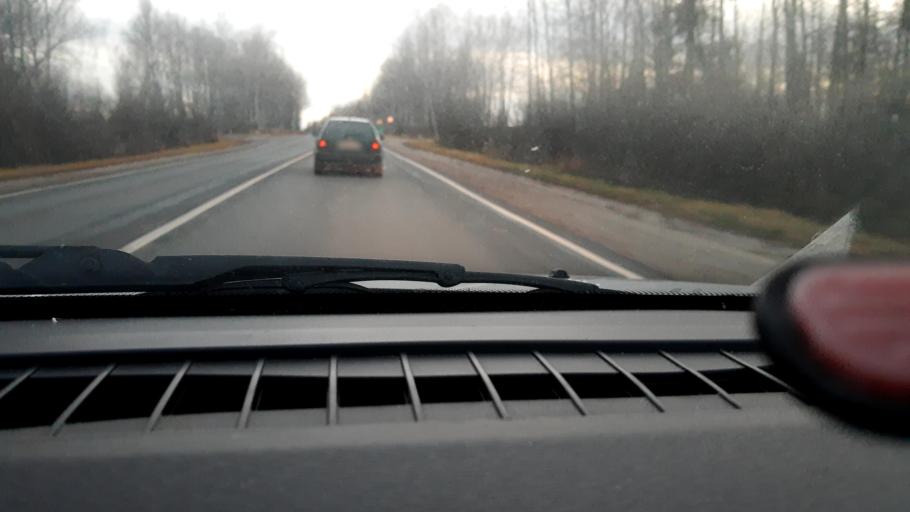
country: RU
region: Nizjnij Novgorod
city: Krasnyye Baki
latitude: 57.0603
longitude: 45.1371
